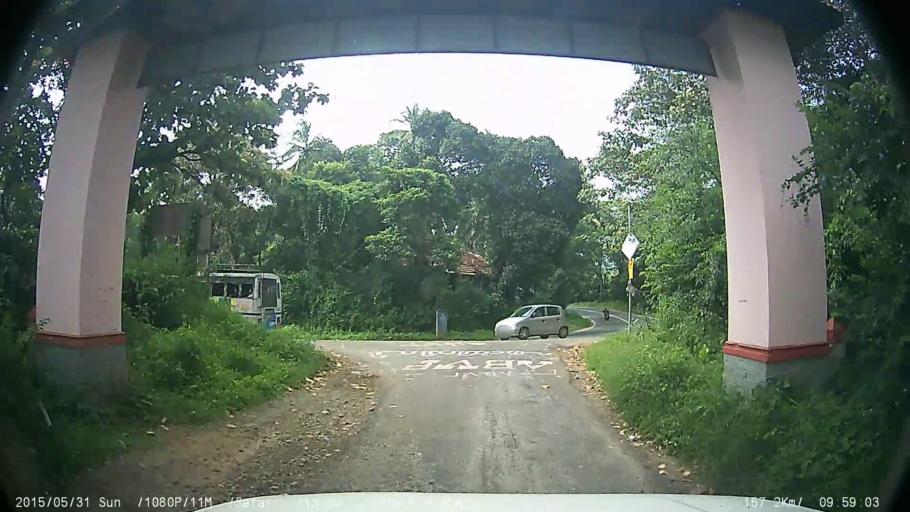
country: IN
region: Kerala
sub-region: Wayanad
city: Kalpetta
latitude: 11.5903
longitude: 76.0659
